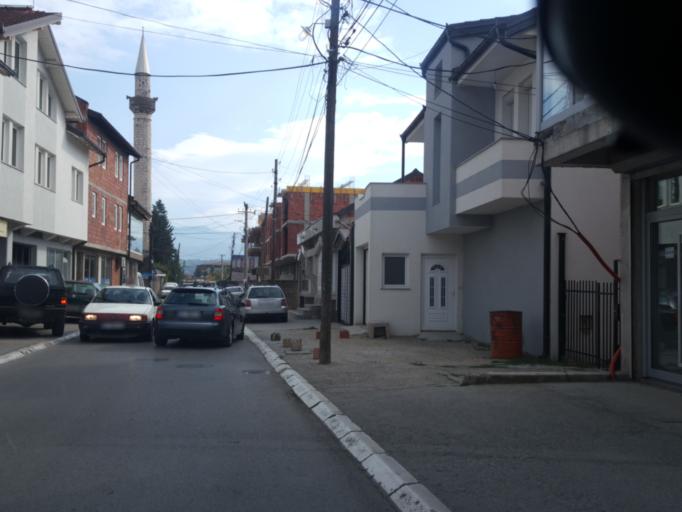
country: XK
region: Gjakova
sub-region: Komuna e Gjakoves
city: Gjakove
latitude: 42.3721
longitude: 20.4297
